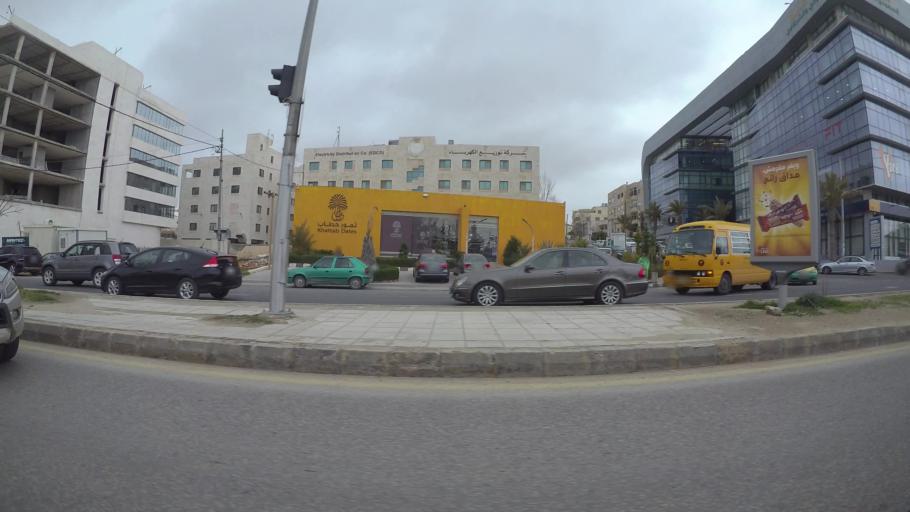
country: JO
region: Amman
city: Al Jubayhah
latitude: 31.9967
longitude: 35.8405
